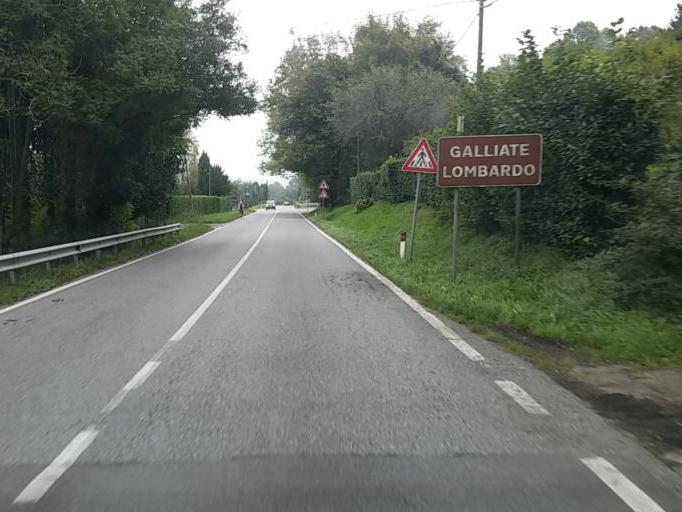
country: IT
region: Lombardy
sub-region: Provincia di Varese
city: Galliate Lombardo
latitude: 45.7903
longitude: 8.7624
